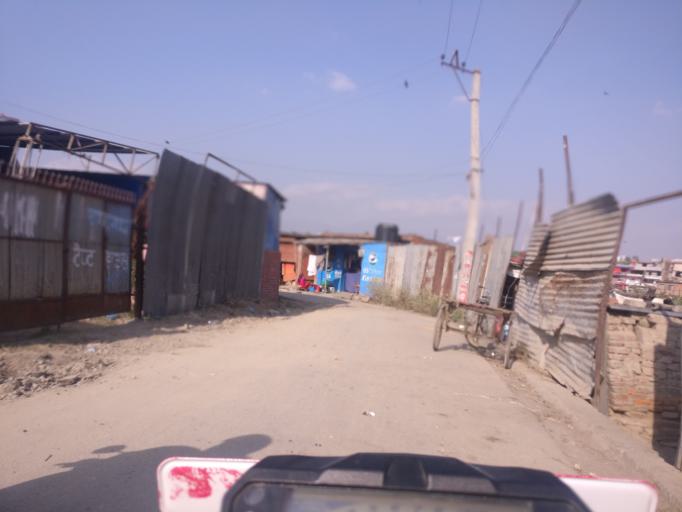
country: NP
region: Central Region
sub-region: Bagmati Zone
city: Patan
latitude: 27.6805
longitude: 85.3293
